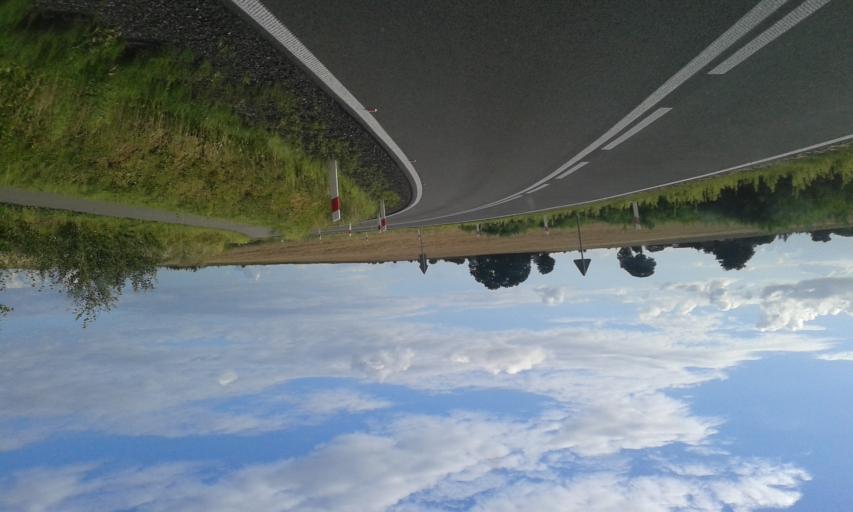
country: PL
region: West Pomeranian Voivodeship
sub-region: Koszalin
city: Koszalin
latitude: 54.1110
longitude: 16.1692
